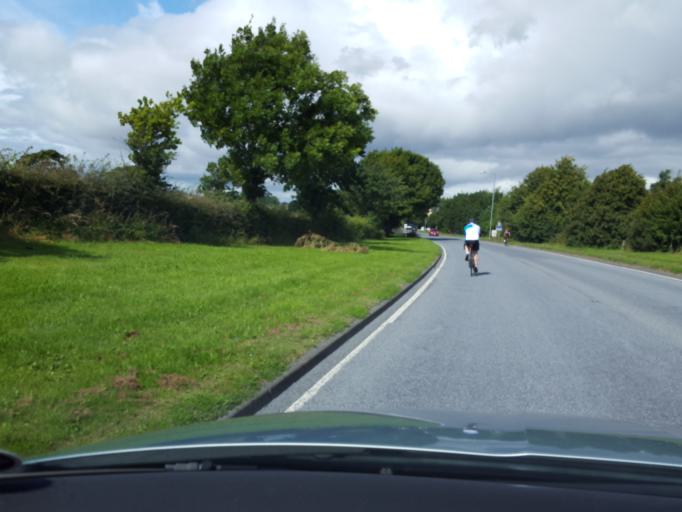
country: GB
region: Scotland
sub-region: Falkirk
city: Bo'ness
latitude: 56.0079
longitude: -3.5802
